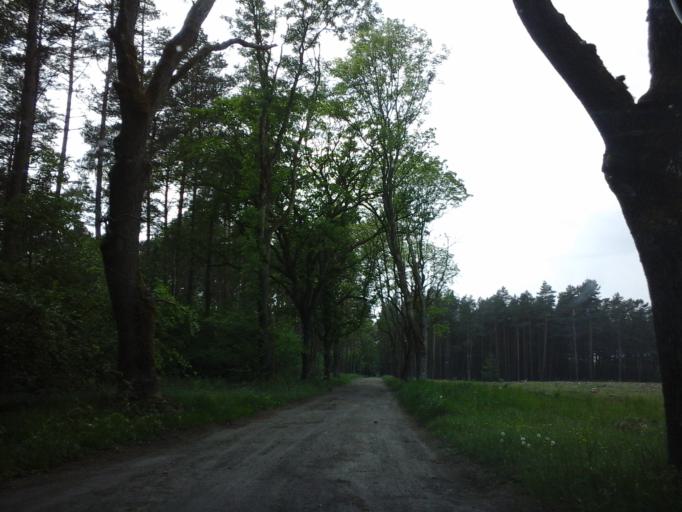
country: PL
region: West Pomeranian Voivodeship
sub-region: Powiat walecki
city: Tuczno
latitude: 53.2218
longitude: 16.0502
